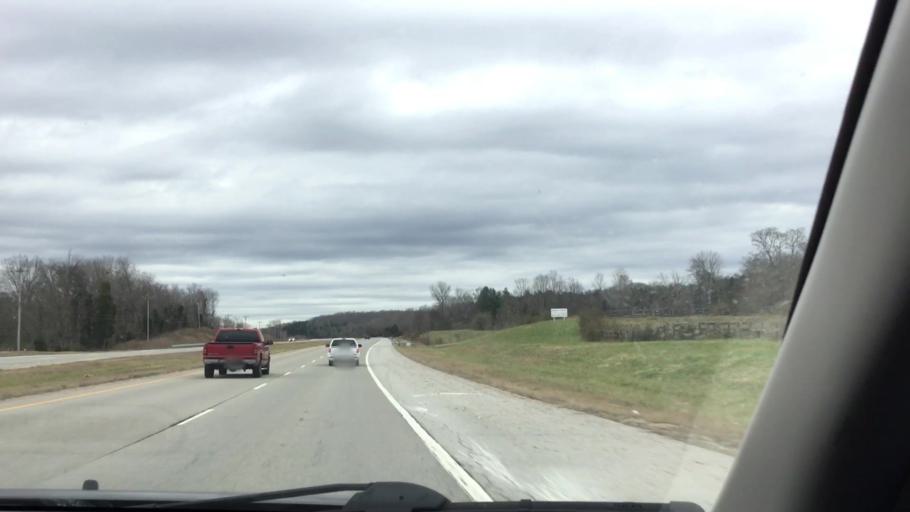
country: US
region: Tennessee
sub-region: Lewis County
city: Hohenwald
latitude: 35.5880
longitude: -87.4481
